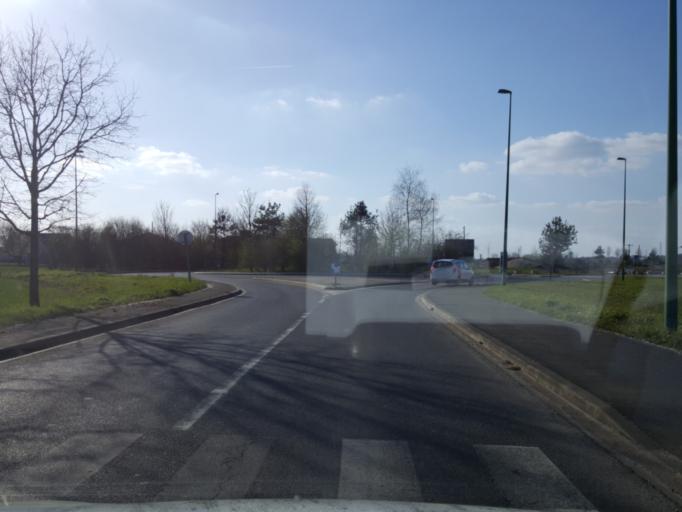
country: FR
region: Ile-de-France
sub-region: Departement des Yvelines
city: Rambouillet
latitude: 48.6217
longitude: 1.8164
